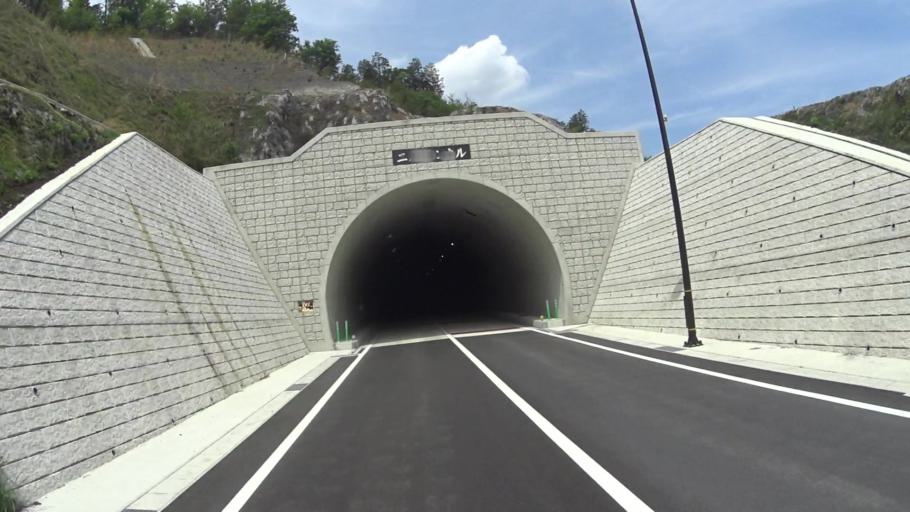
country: JP
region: Kyoto
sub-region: Kyoto-shi
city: Kamigyo-ku
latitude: 35.0951
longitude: 135.7669
